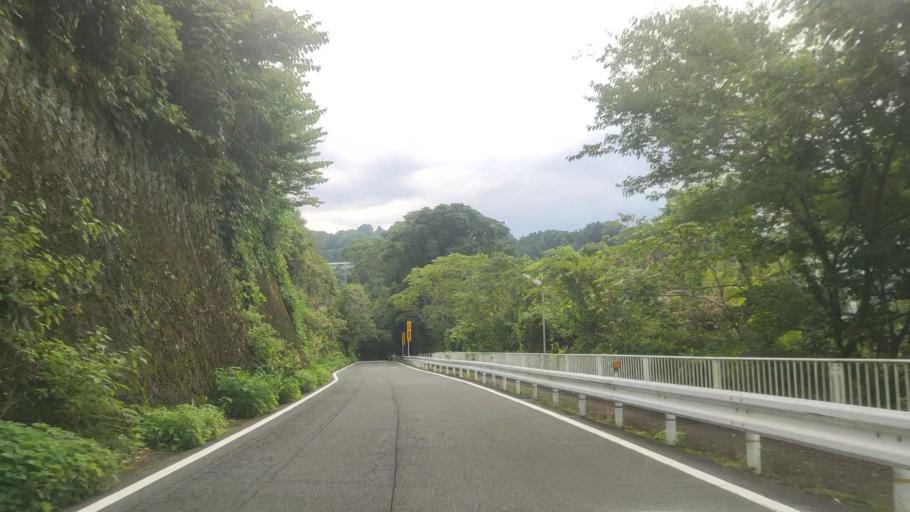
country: JP
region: Wakayama
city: Hashimoto
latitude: 34.2867
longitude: 135.5631
